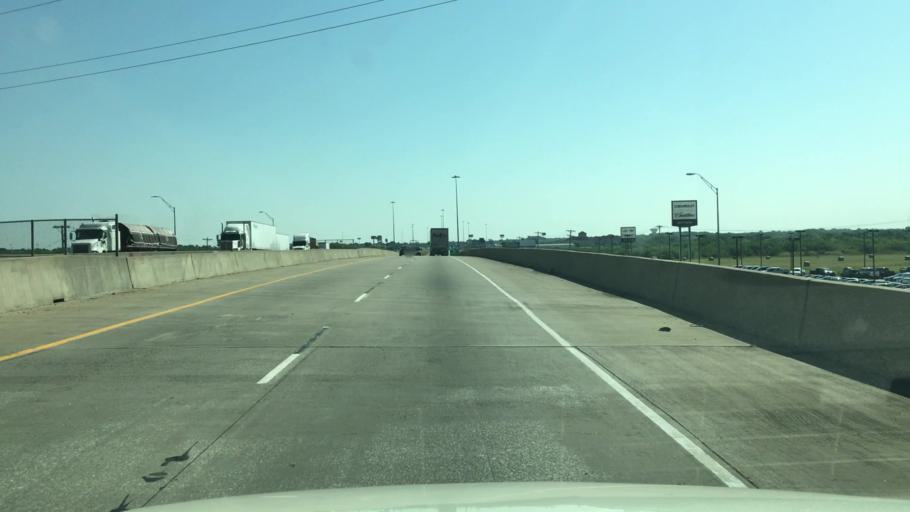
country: US
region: Texas
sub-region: Hunt County
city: Greenville
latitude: 33.0880
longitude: -96.1260
